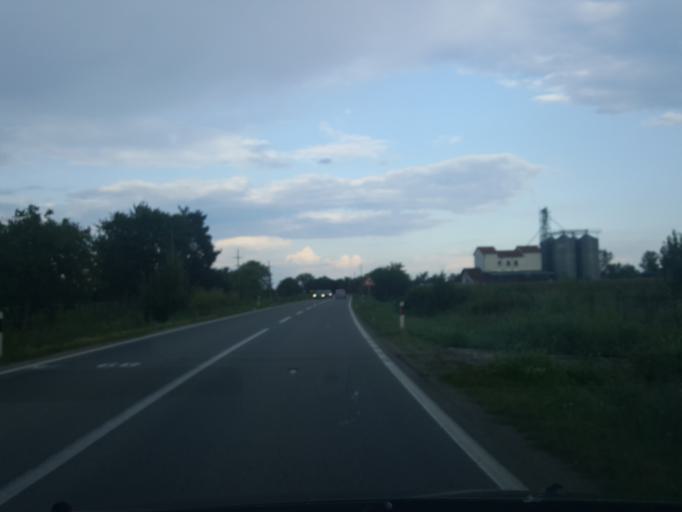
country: RS
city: Zminjak
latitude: 44.7363
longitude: 19.4939
